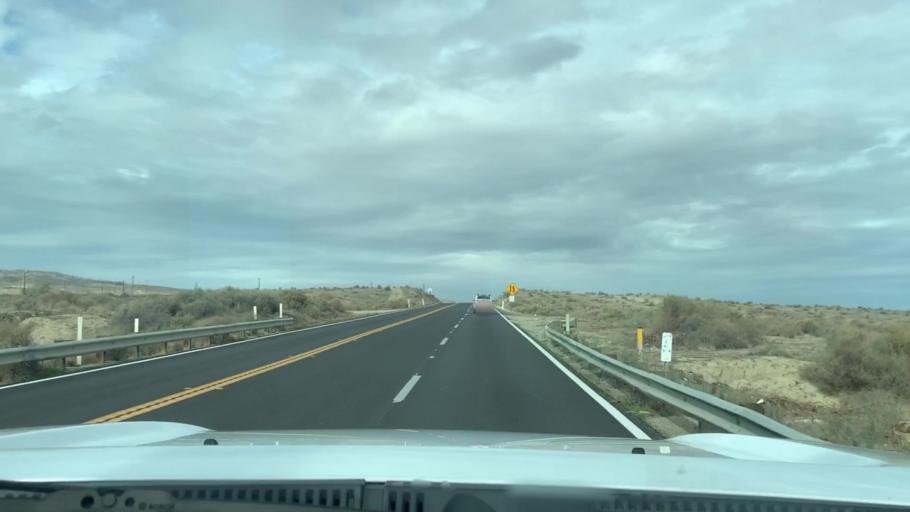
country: US
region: California
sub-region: Kern County
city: Maricopa
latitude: 35.1027
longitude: -119.4174
